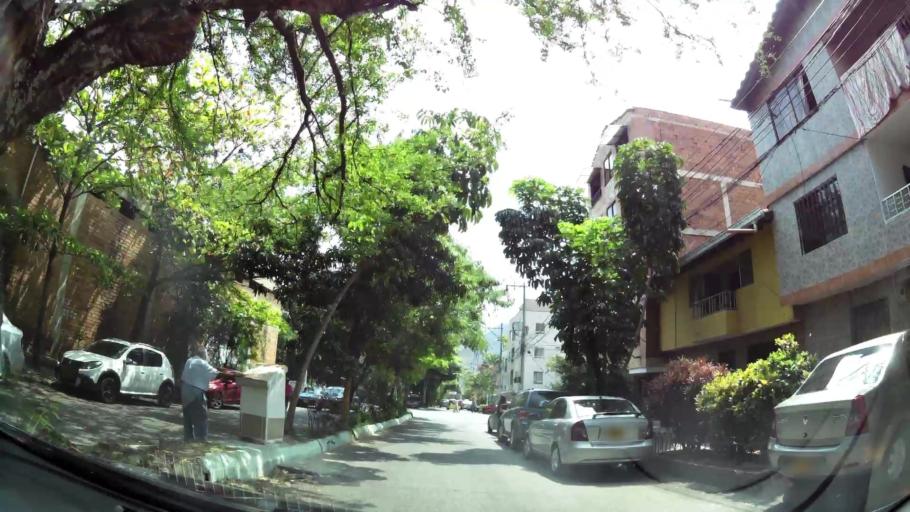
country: CO
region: Antioquia
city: Bello
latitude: 6.3223
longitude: -75.5589
